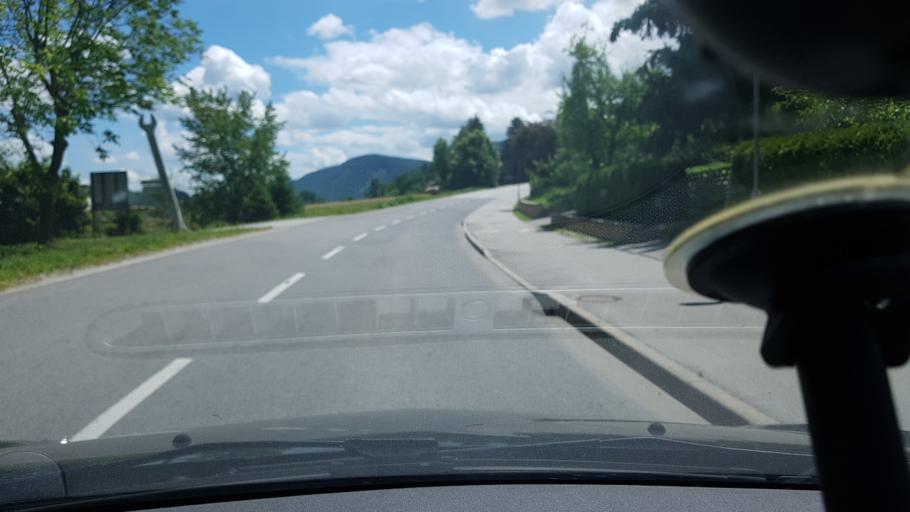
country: SI
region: Zrece
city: Zrece
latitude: 46.3697
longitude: 15.3938
